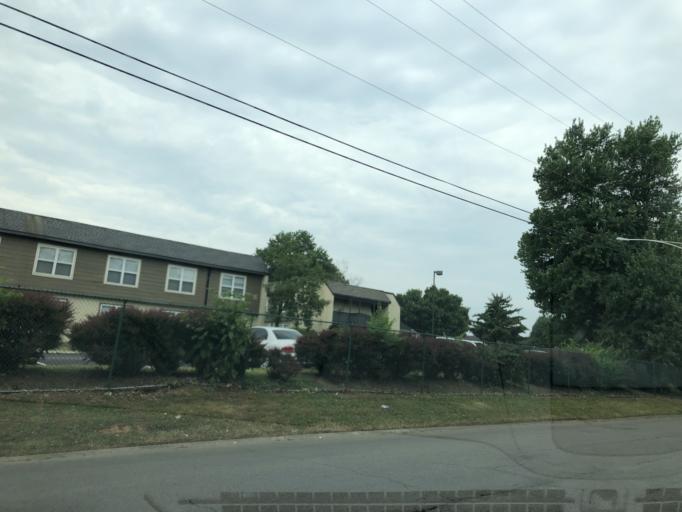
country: US
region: Tennessee
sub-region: Davidson County
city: Oak Hill
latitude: 36.0740
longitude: -86.6886
